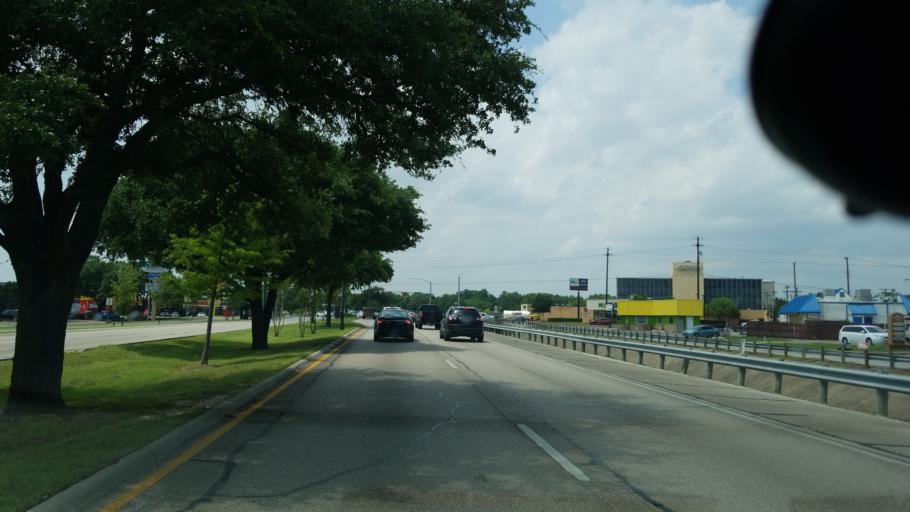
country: US
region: Texas
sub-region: Dallas County
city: Irving
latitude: 32.8210
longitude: -96.9660
